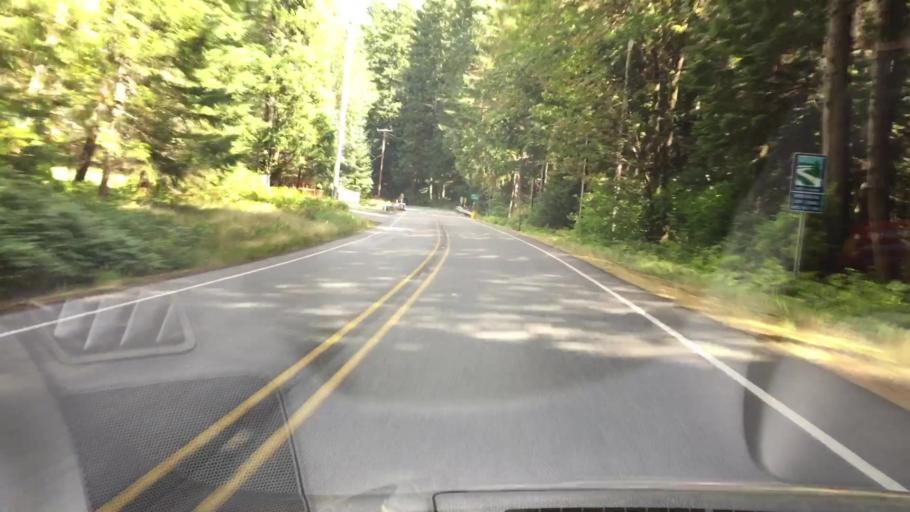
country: US
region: Washington
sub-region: Pierce County
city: Eatonville
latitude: 46.7551
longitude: -121.9631
